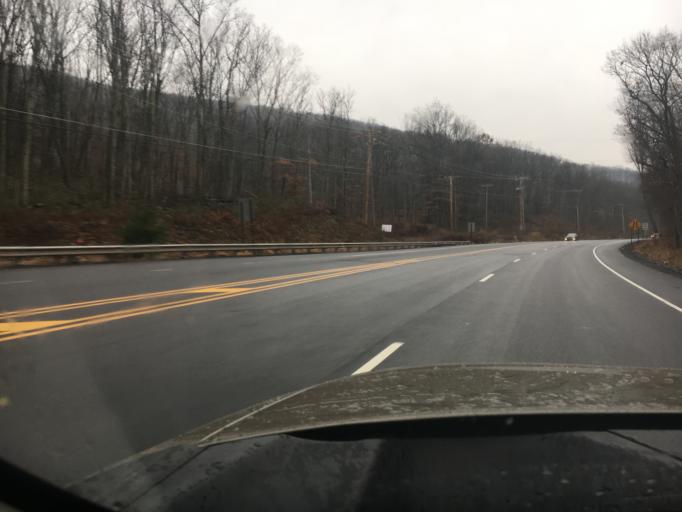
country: US
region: Pennsylvania
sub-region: Luzerne County
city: Oakdale
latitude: 41.0325
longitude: -75.9535
